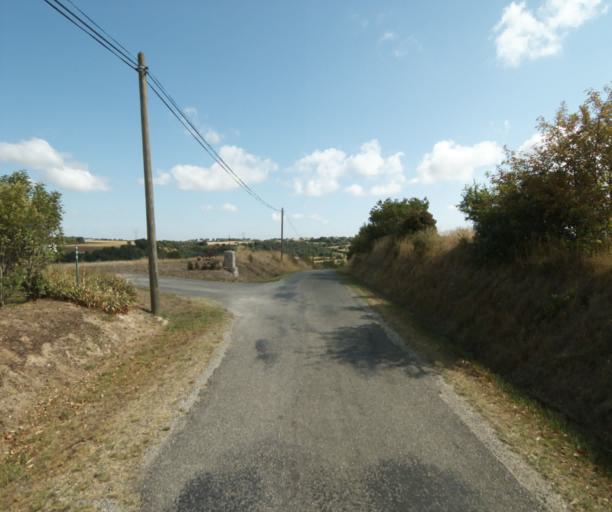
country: FR
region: Midi-Pyrenees
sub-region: Departement de la Haute-Garonne
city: Saint-Felix-Lauragais
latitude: 43.4432
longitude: 1.8233
